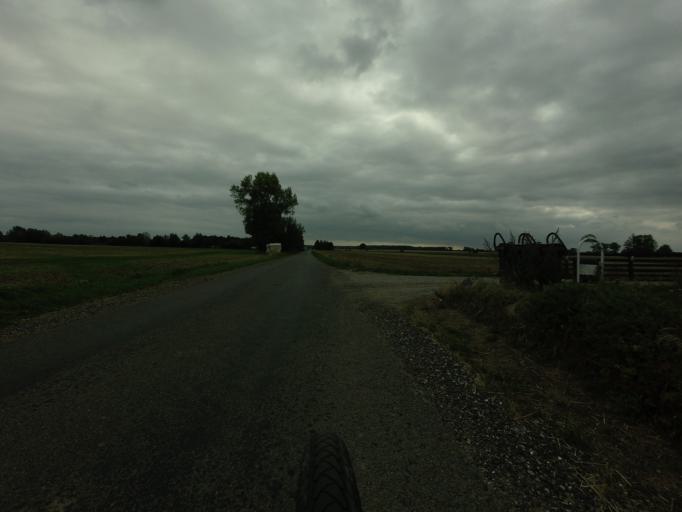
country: DK
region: Zealand
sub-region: Stevns Kommune
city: Store Heddinge
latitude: 55.3373
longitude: 12.3327
